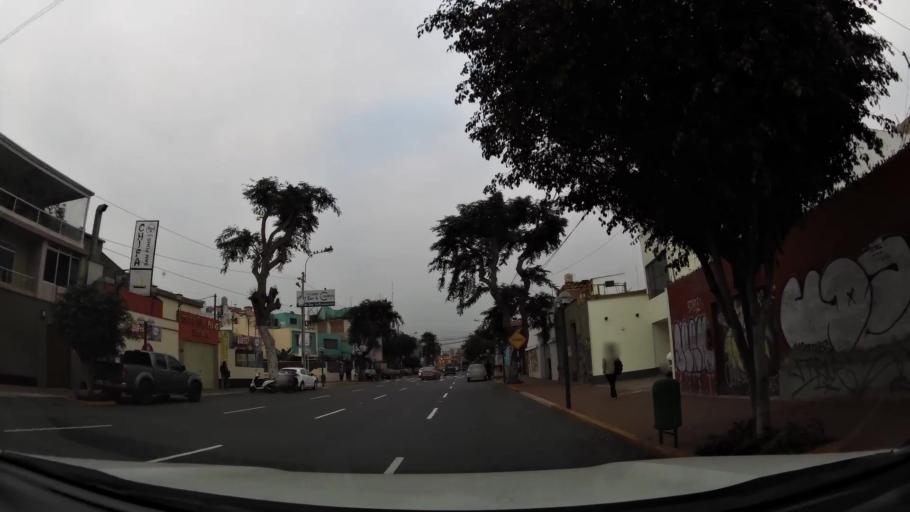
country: PE
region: Lima
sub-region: Lima
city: Surco
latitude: -12.1416
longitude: -77.0200
